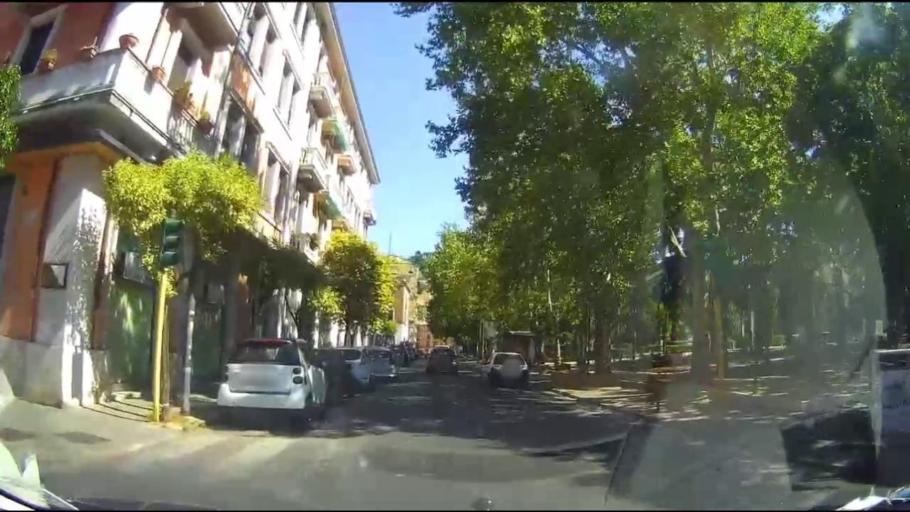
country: IT
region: Calabria
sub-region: Provincia di Cosenza
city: Cosenza
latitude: 39.2949
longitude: 16.2540
